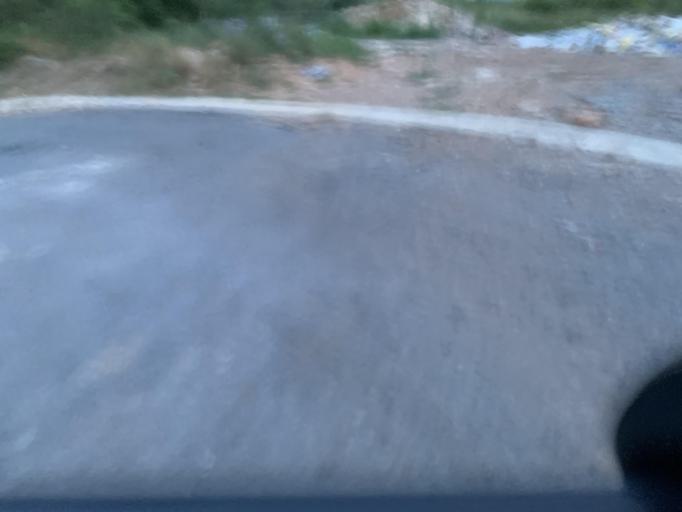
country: MX
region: Nuevo Leon
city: Santiago
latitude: 25.5091
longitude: -100.1831
